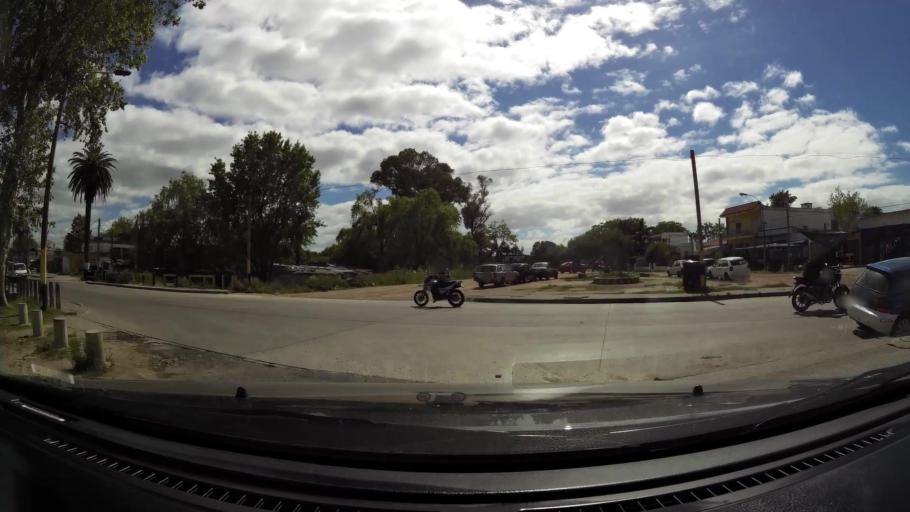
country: UY
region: Canelones
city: Paso de Carrasco
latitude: -34.8837
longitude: -56.1113
